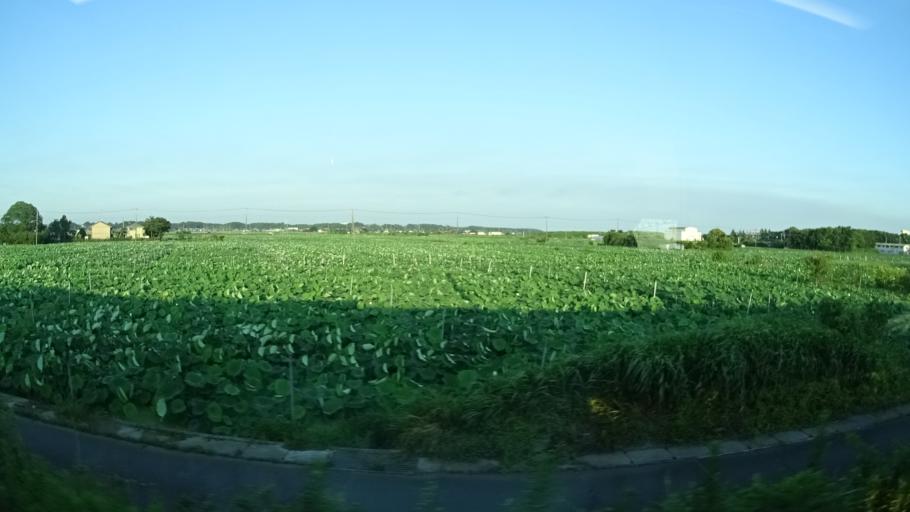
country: JP
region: Ibaraki
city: Ami
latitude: 36.0917
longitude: 140.2136
